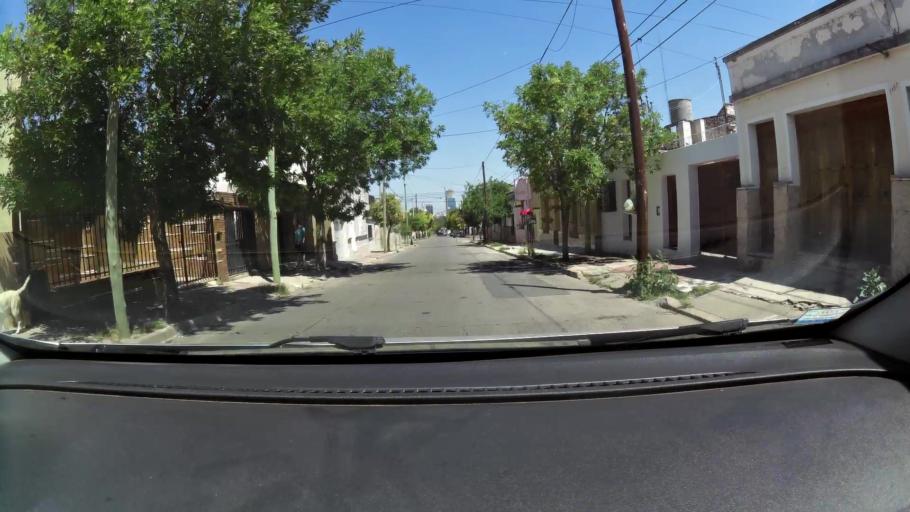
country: AR
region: Cordoba
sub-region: Departamento de Capital
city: Cordoba
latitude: -31.3937
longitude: -64.1986
